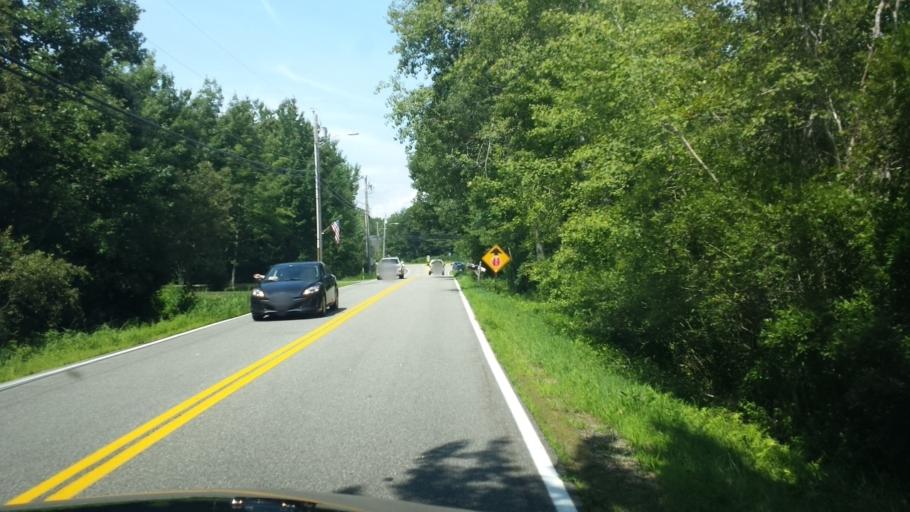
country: US
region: Maine
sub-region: York County
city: Old Orchard Beach
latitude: 43.4238
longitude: -70.3863
